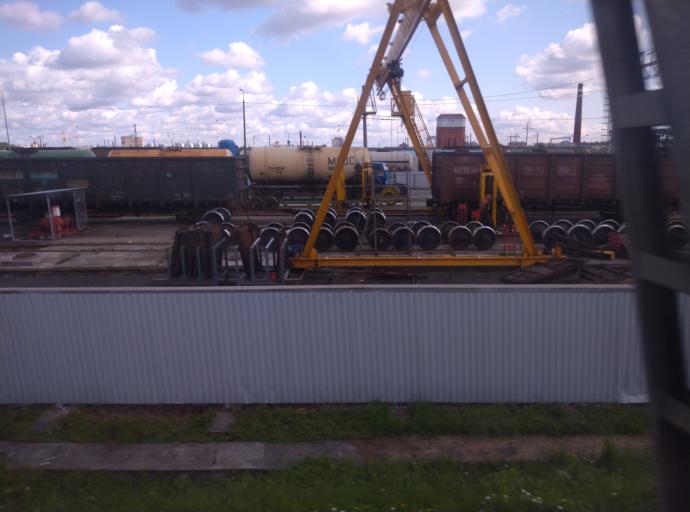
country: RU
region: St.-Petersburg
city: Obukhovo
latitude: 59.8719
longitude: 30.4176
